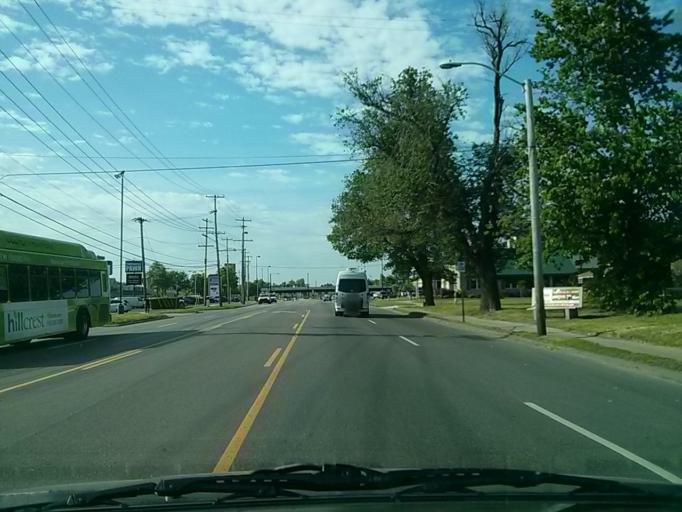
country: US
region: Oklahoma
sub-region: Tulsa County
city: Tulsa
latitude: 36.0928
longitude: -95.9758
